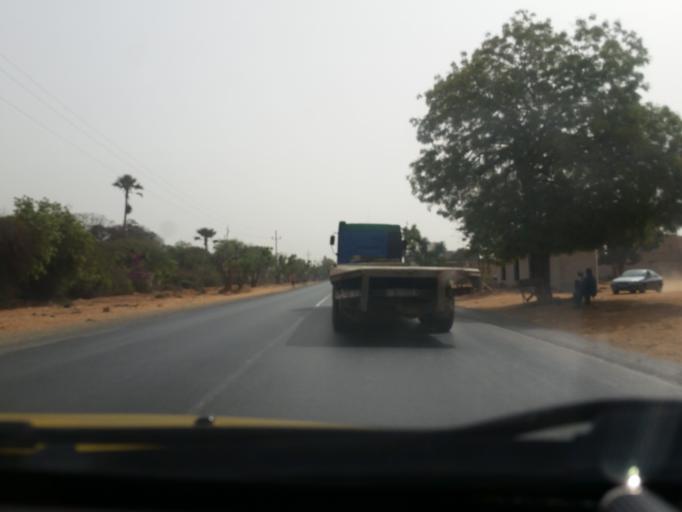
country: SN
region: Thies
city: Pout
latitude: 14.7491
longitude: -17.1306
